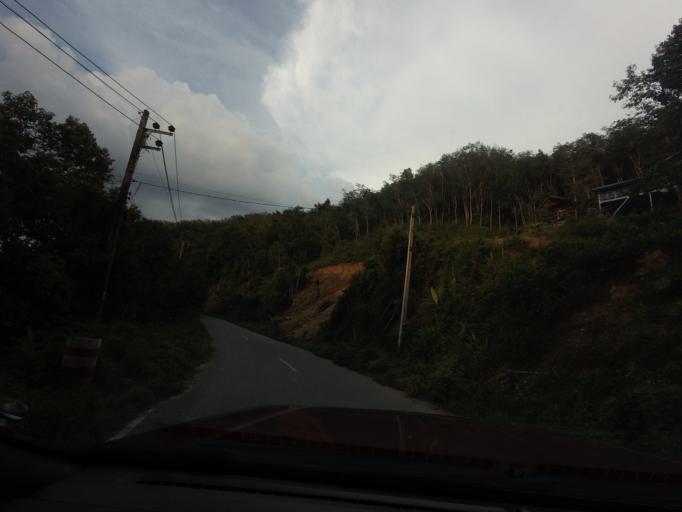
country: TH
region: Yala
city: Than To
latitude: 6.0083
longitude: 101.2278
